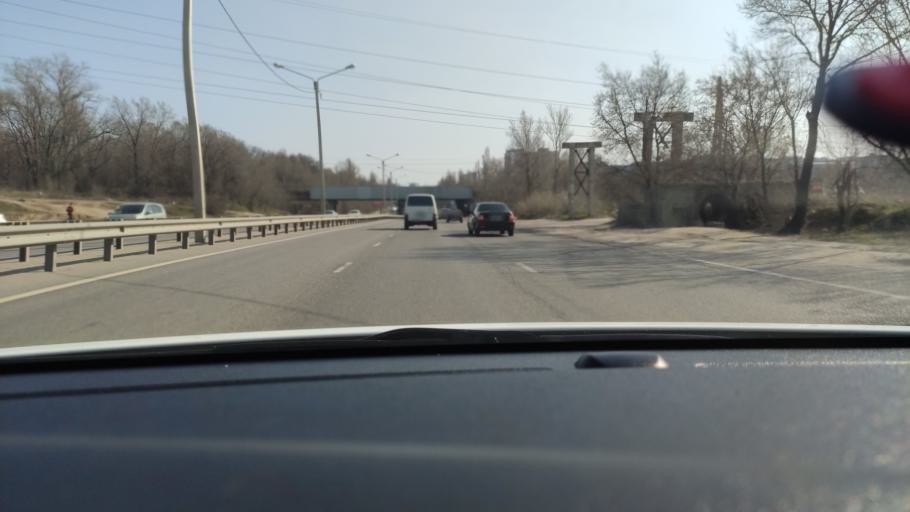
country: RU
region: Voronezj
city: Pridonskoy
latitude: 51.6653
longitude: 39.1255
